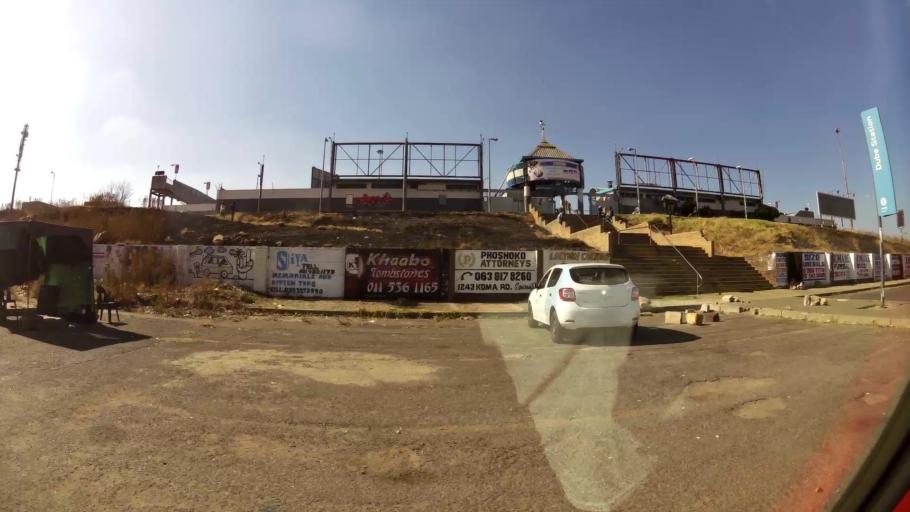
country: ZA
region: Gauteng
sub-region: City of Johannesburg Metropolitan Municipality
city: Soweto
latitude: -26.2335
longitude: 27.8921
